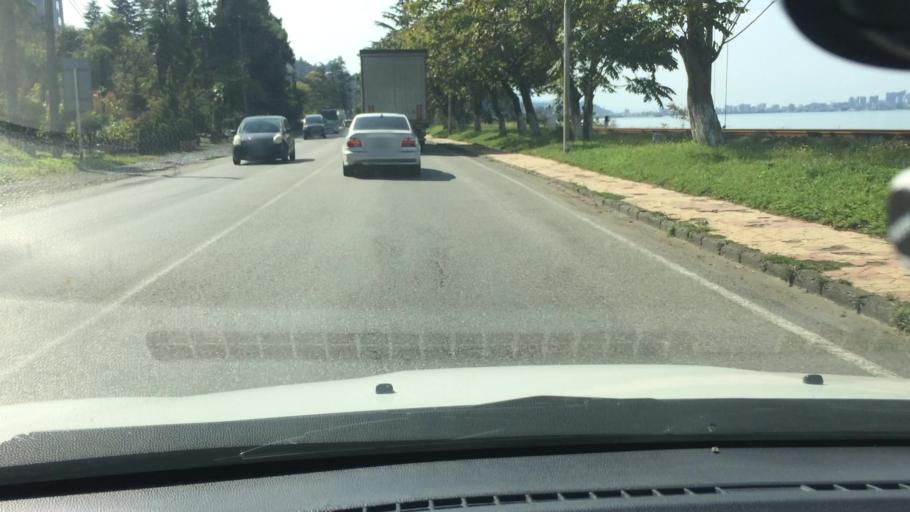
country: GE
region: Ajaria
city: Makhinjauri
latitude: 41.6823
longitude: 41.6991
